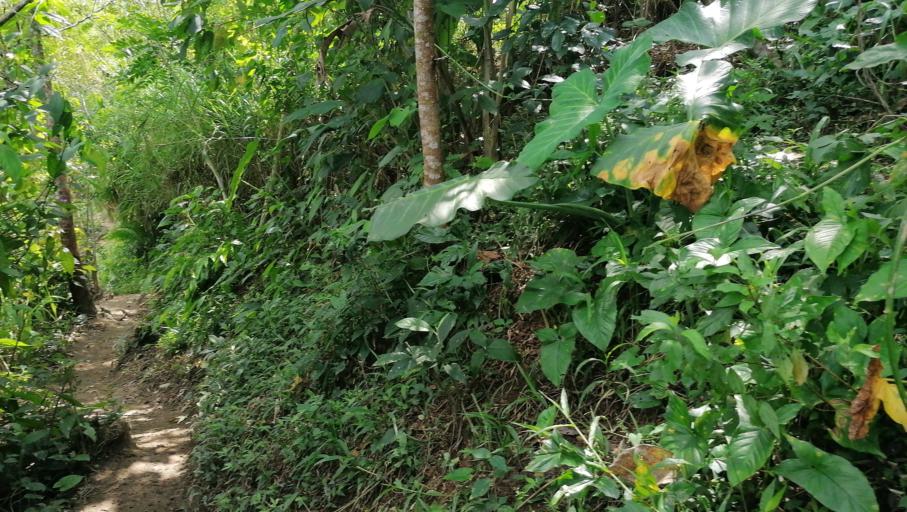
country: MX
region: Chiapas
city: Ocotepec
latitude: 17.2951
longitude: -93.2271
